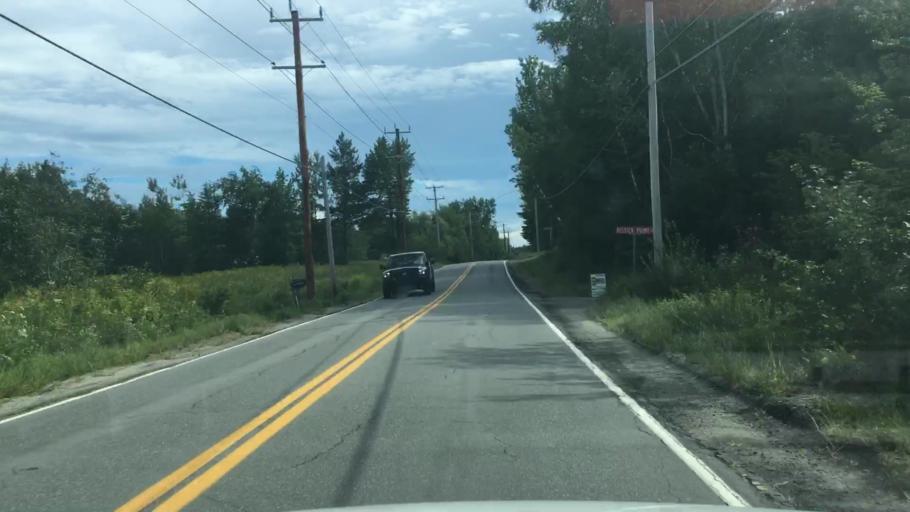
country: US
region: Maine
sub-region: Hancock County
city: Ellsworth
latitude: 44.4894
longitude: -68.4201
